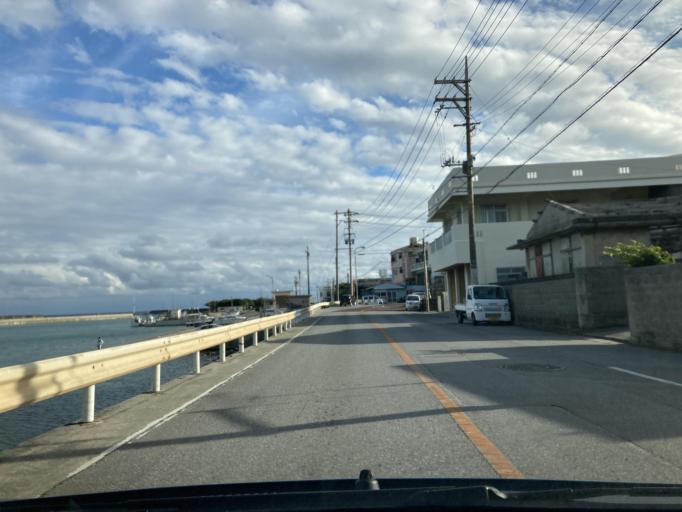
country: JP
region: Okinawa
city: Itoman
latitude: 26.1282
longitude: 127.7603
